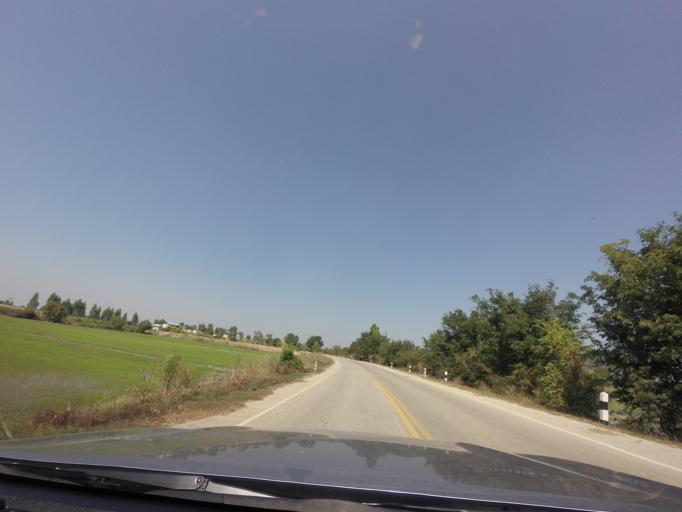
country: TH
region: Sukhothai
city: Sukhothai
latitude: 17.0886
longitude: 99.7906
